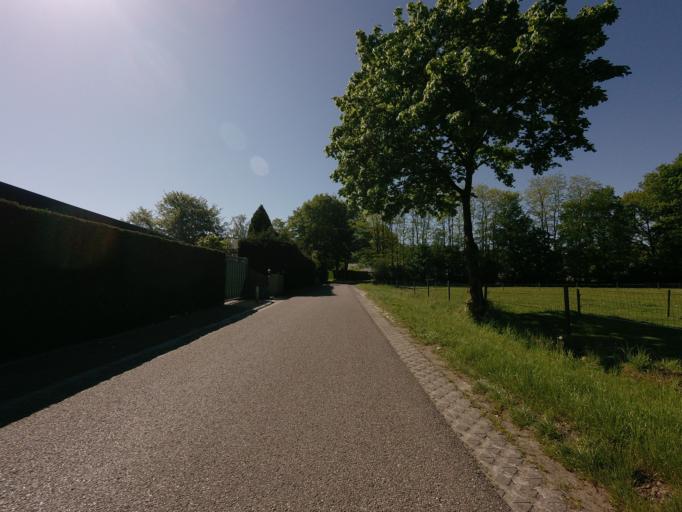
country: NL
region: North Brabant
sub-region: Gemeente Rucphen
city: Rucphen
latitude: 51.5776
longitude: 4.5578
